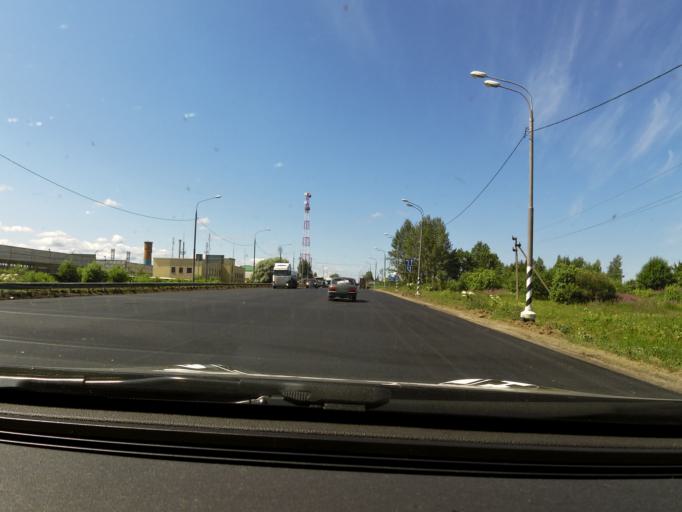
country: RU
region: Novgorod
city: Valday
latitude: 57.9520
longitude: 33.2886
